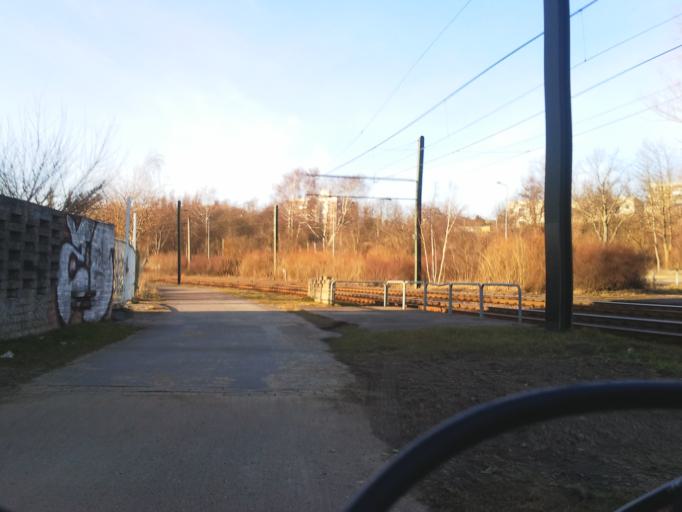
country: DE
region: Mecklenburg-Vorpommern
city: Dierkow-West
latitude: 54.0992
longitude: 12.1564
